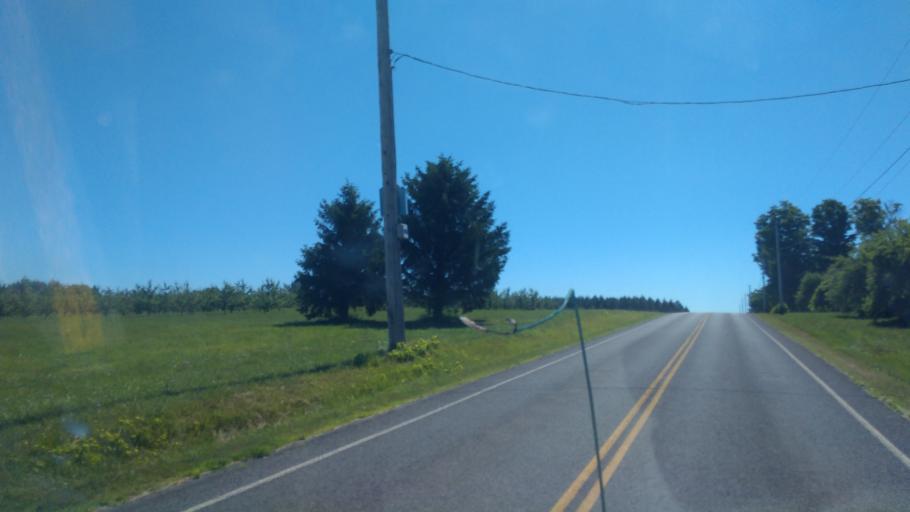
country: US
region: New York
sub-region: Wayne County
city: Sodus
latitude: 43.2772
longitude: -77.1189
